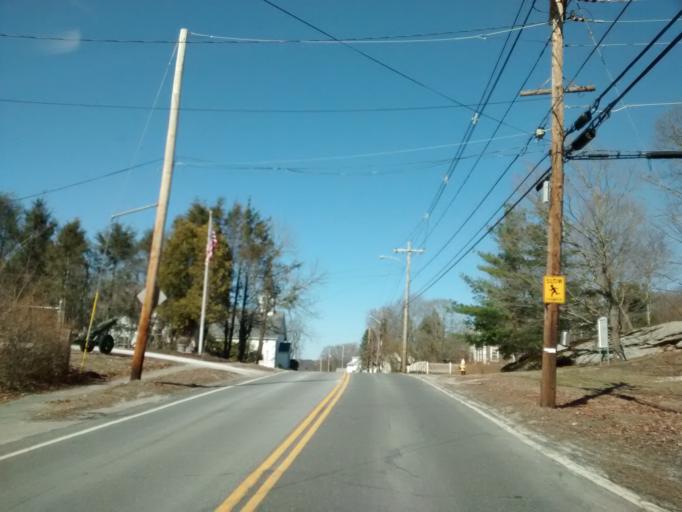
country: US
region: Massachusetts
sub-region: Worcester County
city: Whitinsville
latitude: 42.1328
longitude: -71.6724
